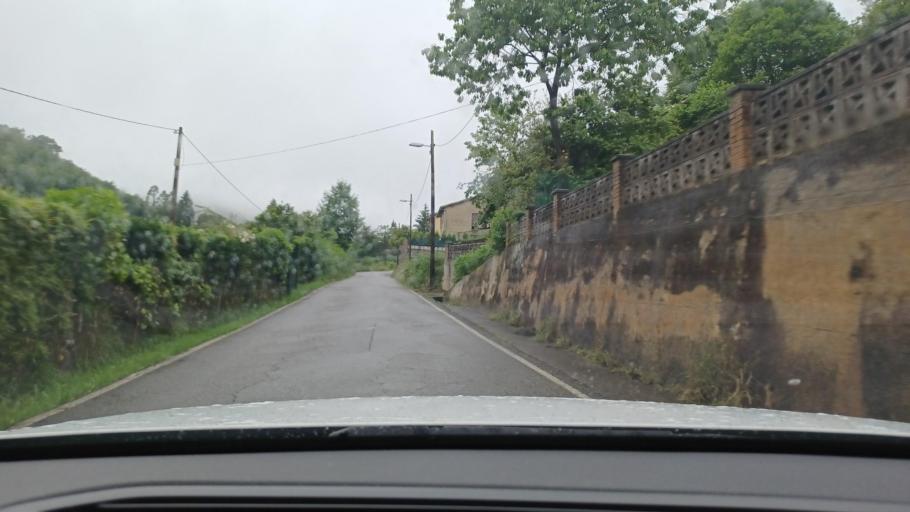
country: ES
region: Asturias
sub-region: Province of Asturias
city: Castandiello
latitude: 43.3043
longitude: -5.9338
